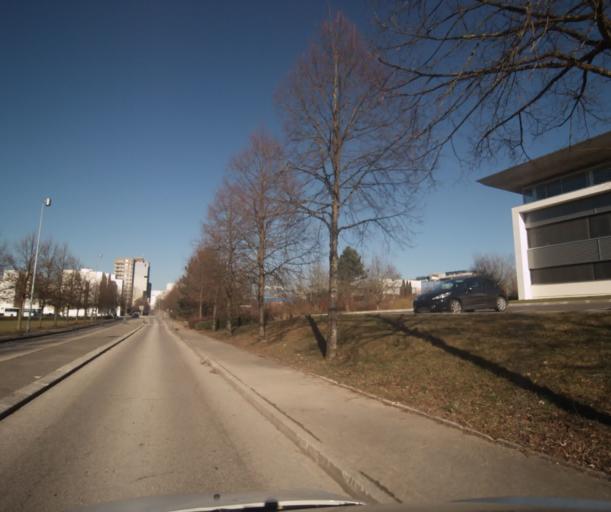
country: FR
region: Franche-Comte
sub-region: Departement du Doubs
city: Avanne-Aveney
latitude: 47.2159
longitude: 5.9673
